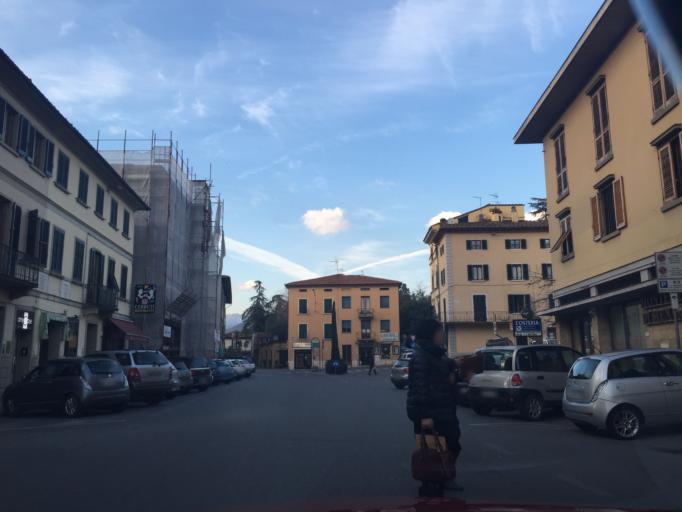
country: IT
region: Tuscany
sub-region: Provincia di Pistoia
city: Monsummano Terme
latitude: 43.8707
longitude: 10.8140
